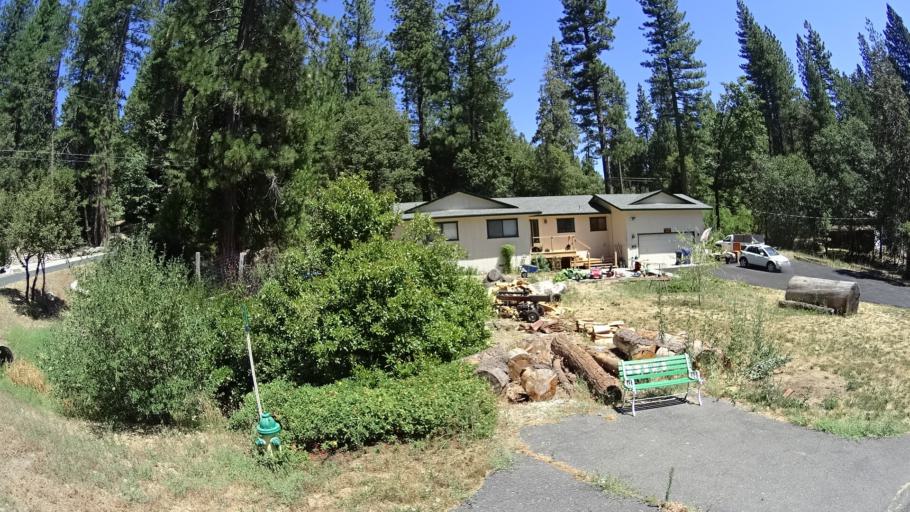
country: US
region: California
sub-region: Calaveras County
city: Forest Meadows
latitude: 38.2071
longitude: -120.3765
